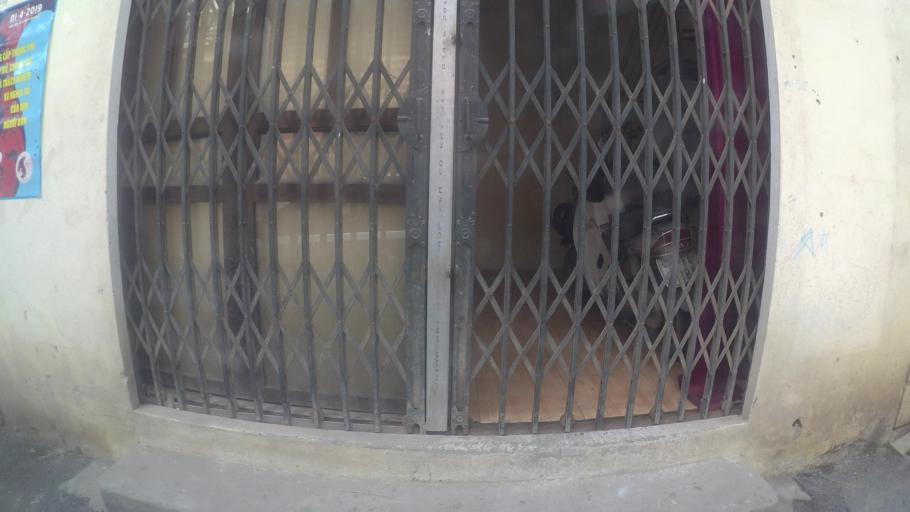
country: VN
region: Ha Noi
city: Tay Ho
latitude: 21.0881
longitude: 105.8029
